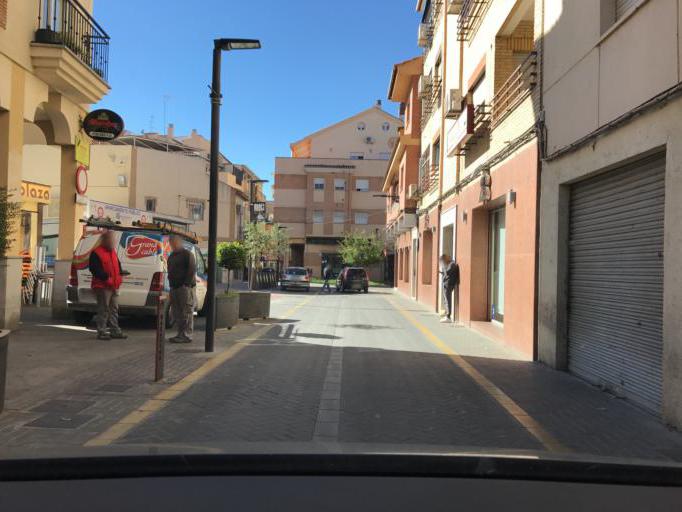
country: ES
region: Andalusia
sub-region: Provincia de Granada
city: Maracena
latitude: 37.2086
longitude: -3.6341
